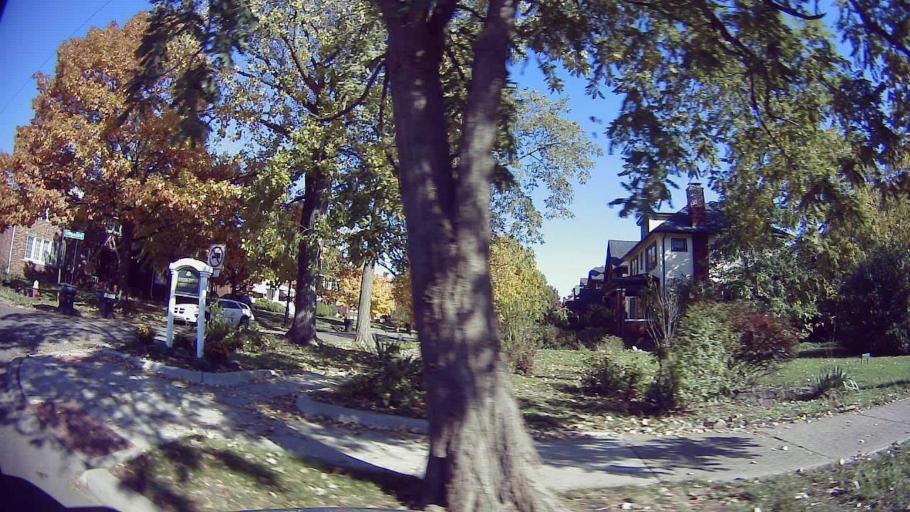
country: US
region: Michigan
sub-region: Wayne County
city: Highland Park
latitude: 42.3756
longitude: -83.1101
